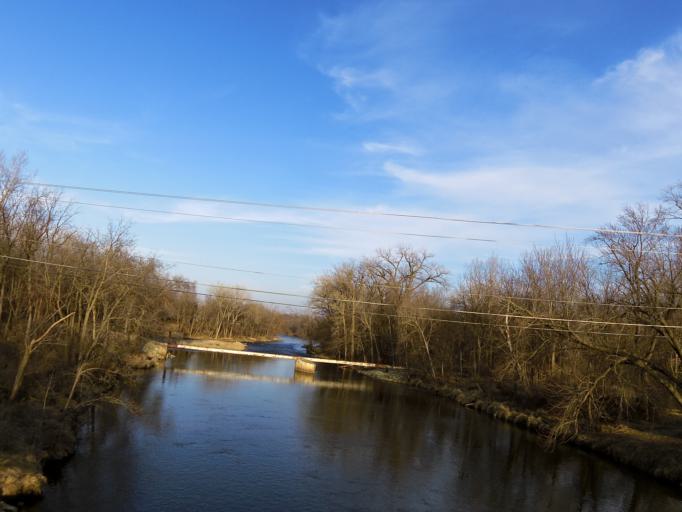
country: US
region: Minnesota
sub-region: Goodhue County
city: Cannon Falls
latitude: 44.5136
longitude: -92.9043
